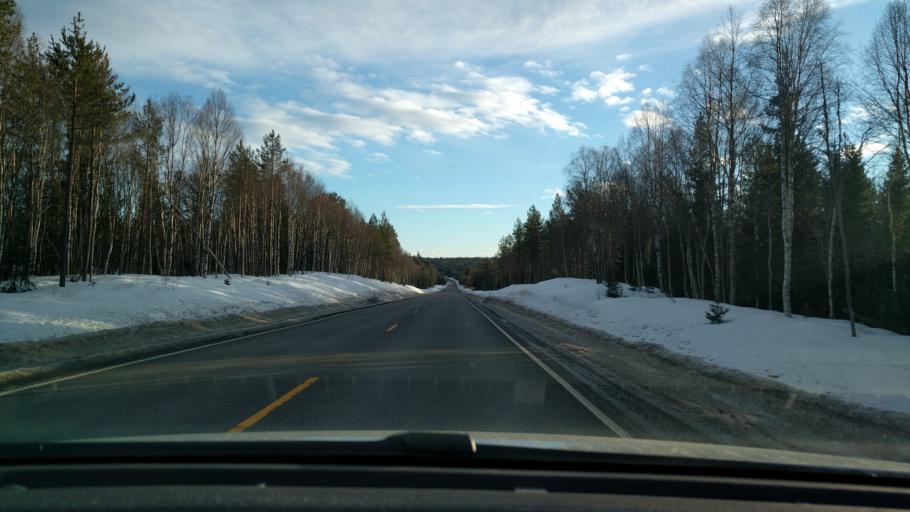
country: NO
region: Hedmark
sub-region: Elverum
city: Elverum
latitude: 61.0379
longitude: 11.8702
